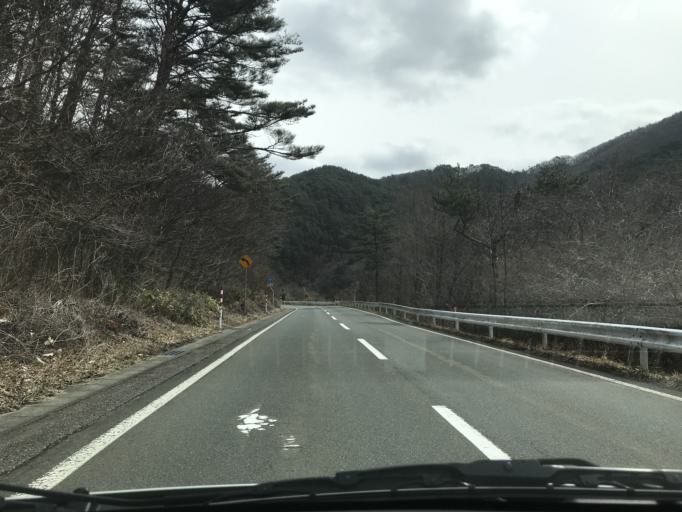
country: JP
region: Iwate
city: Tono
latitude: 39.2979
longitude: 141.3642
